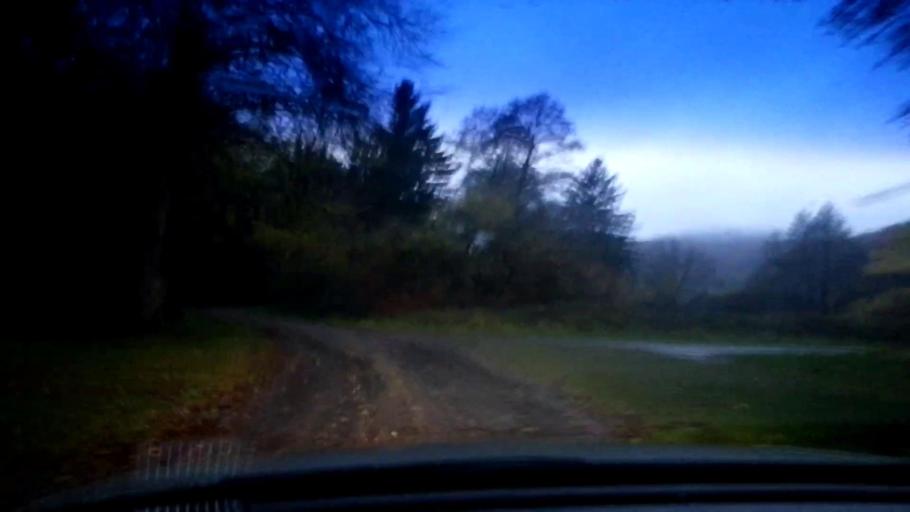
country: DE
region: Bavaria
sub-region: Upper Franconia
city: Schesslitz
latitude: 49.9446
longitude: 11.0632
